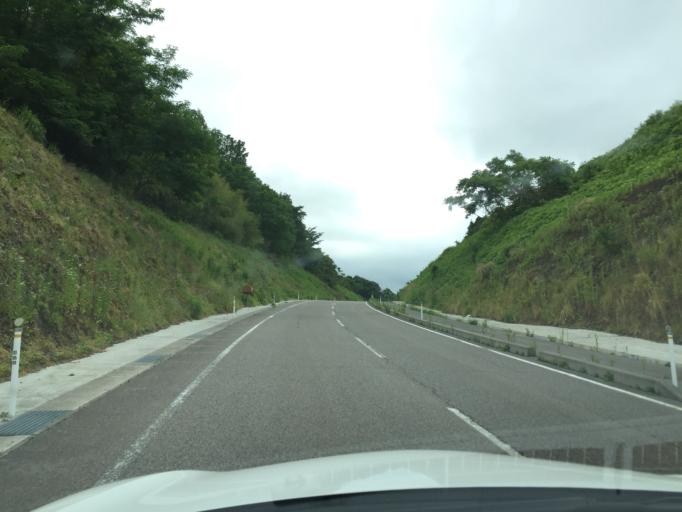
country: JP
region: Fukushima
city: Miharu
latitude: 37.4418
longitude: 140.5107
